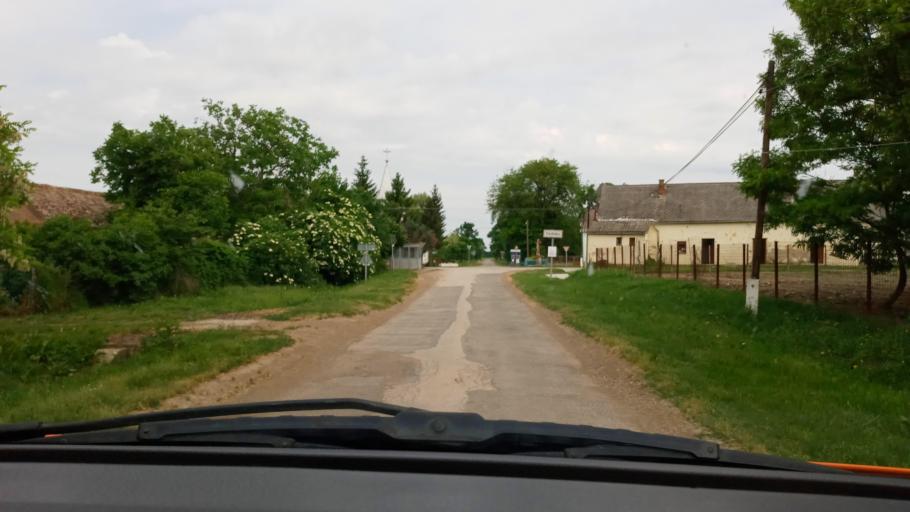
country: HU
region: Baranya
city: Vajszlo
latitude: 45.9281
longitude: 18.0221
